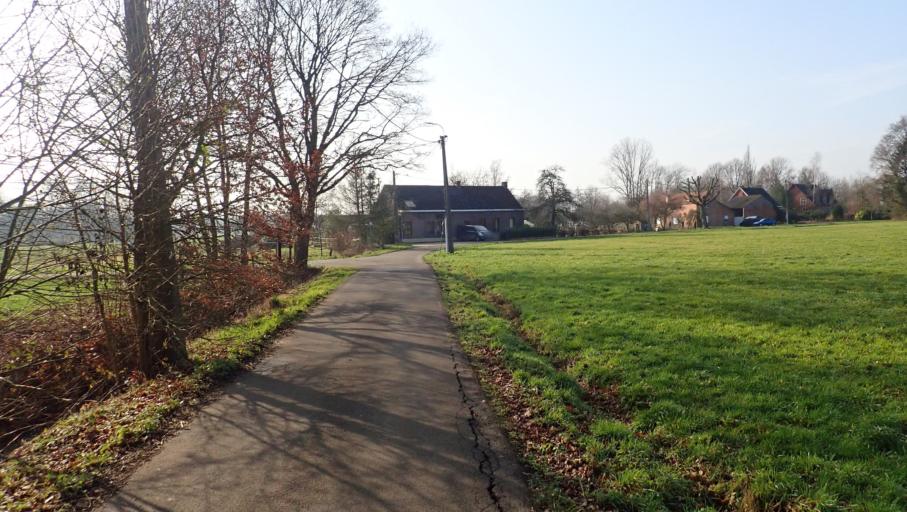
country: BE
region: Flanders
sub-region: Provincie Antwerpen
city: Putte
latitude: 51.0363
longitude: 4.6464
